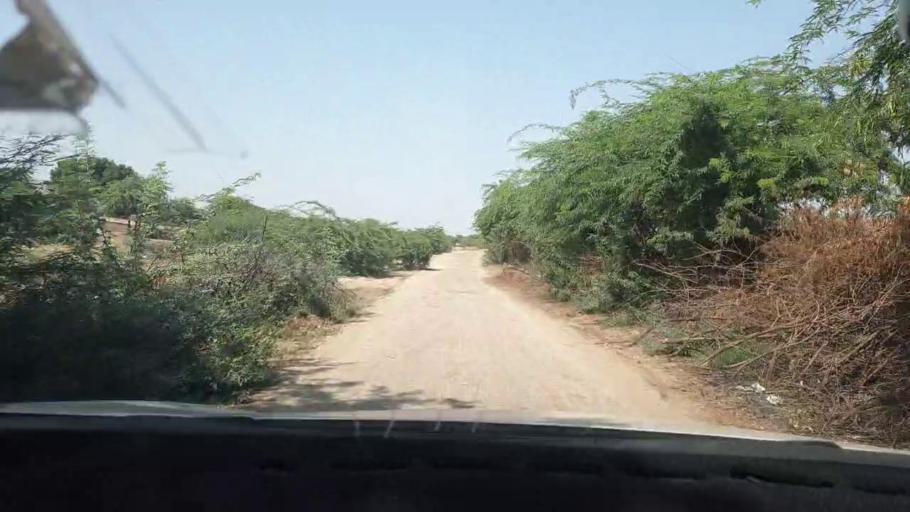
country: PK
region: Sindh
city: Tando Mittha Khan
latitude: 25.8779
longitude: 69.3870
